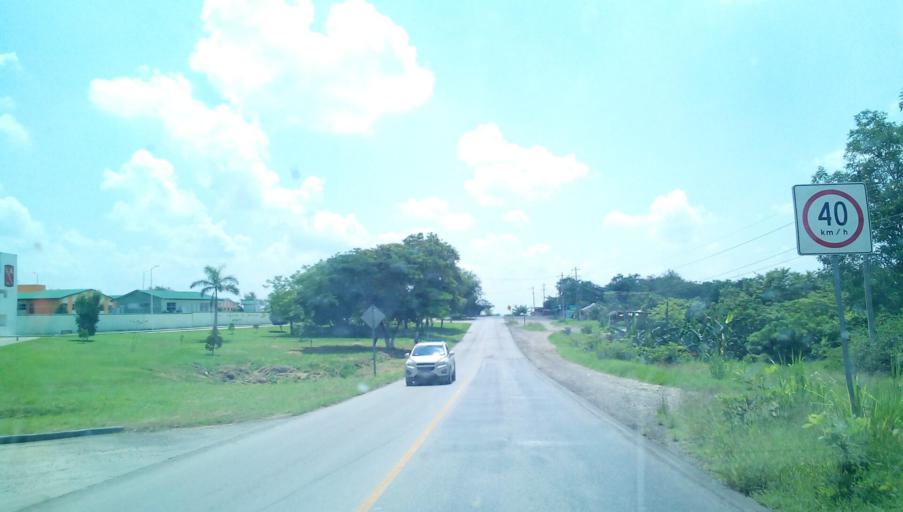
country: MX
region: Veracruz
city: Tempoal de Sanchez
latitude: 21.5878
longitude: -98.3651
